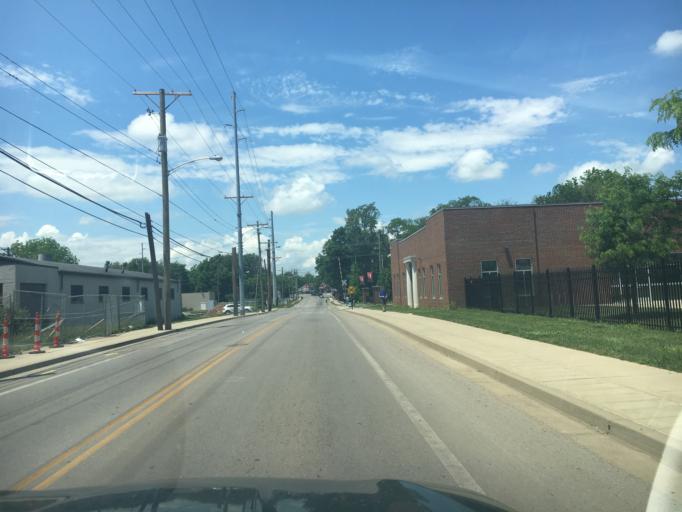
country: US
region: Kentucky
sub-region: Fayette County
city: Mount Vernon
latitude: 38.0578
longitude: -84.4980
